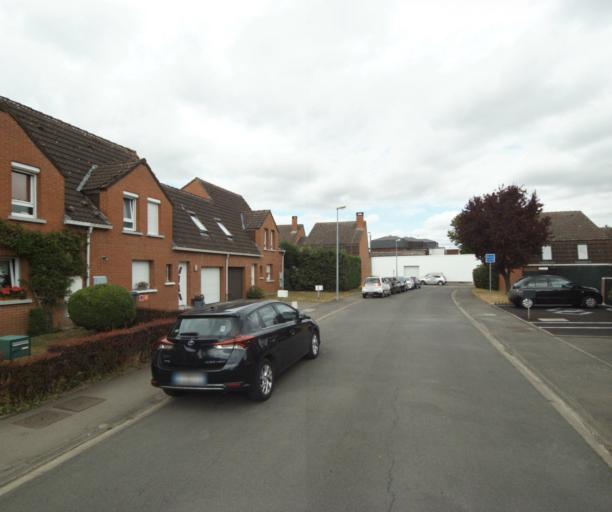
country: FR
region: Nord-Pas-de-Calais
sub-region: Departement du Nord
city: Linselles
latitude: 50.7429
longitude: 3.0863
